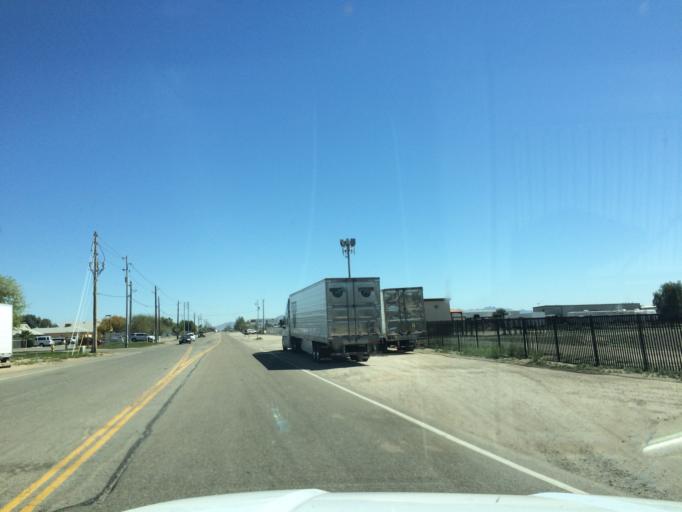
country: US
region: Arizona
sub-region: Yuma County
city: Yuma
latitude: 32.6551
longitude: -114.5810
